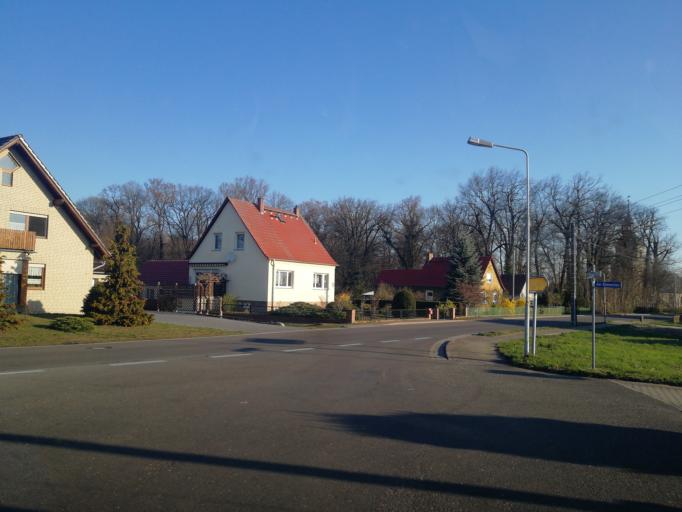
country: DE
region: Brandenburg
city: Drahnsdorf
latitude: 51.9174
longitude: 13.5938
